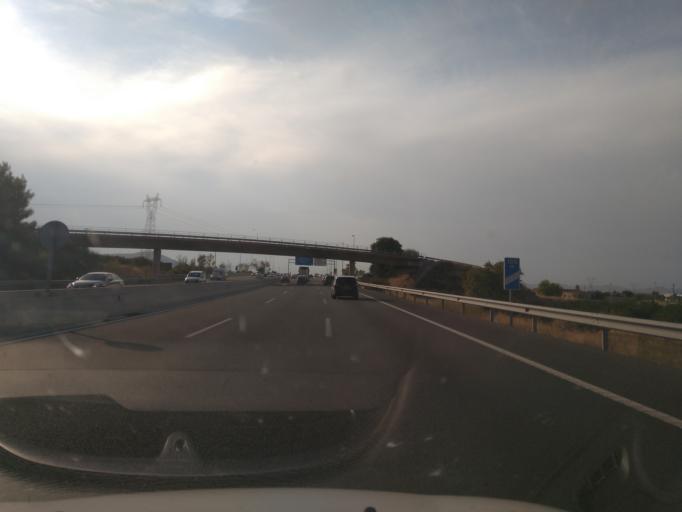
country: ES
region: Valencia
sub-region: Provincia de Valencia
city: Torrent
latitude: 39.4147
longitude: -0.5046
